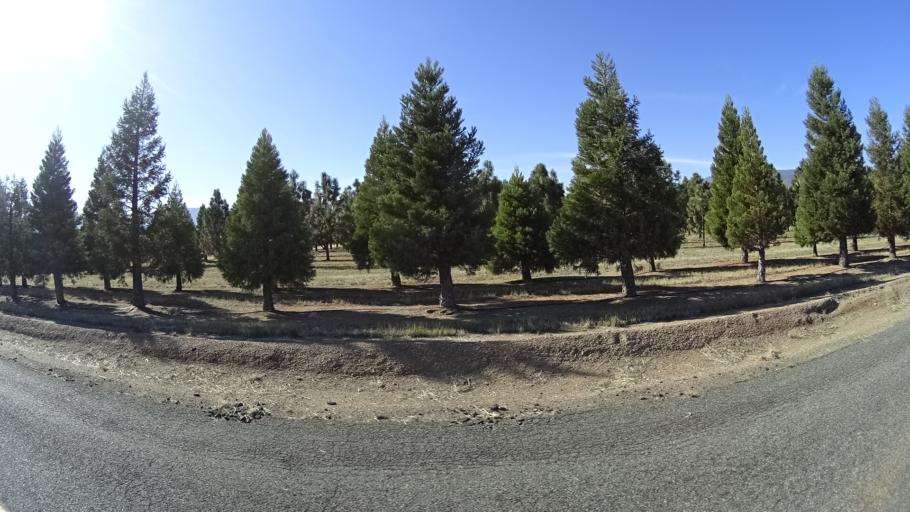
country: US
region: California
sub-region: Siskiyou County
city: Montague
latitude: 41.5546
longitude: -122.5455
